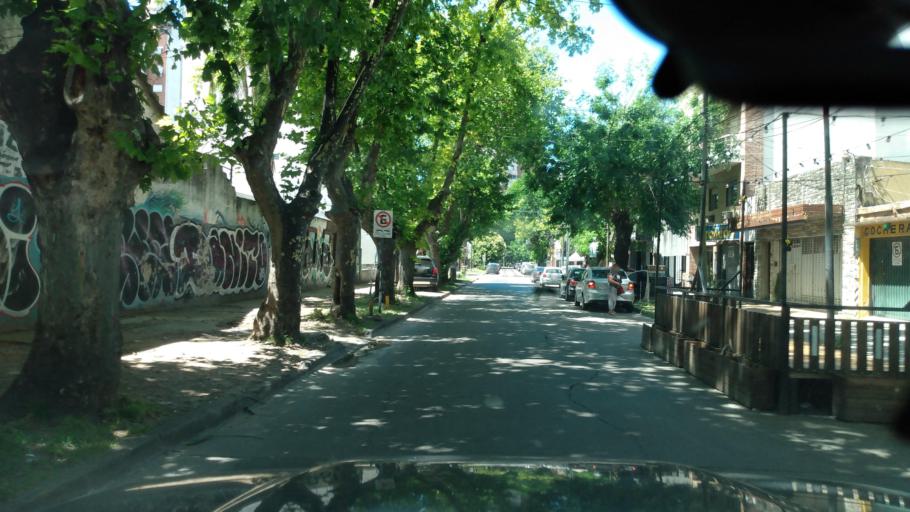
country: AR
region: Buenos Aires
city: Hurlingham
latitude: -34.5429
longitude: -58.7068
